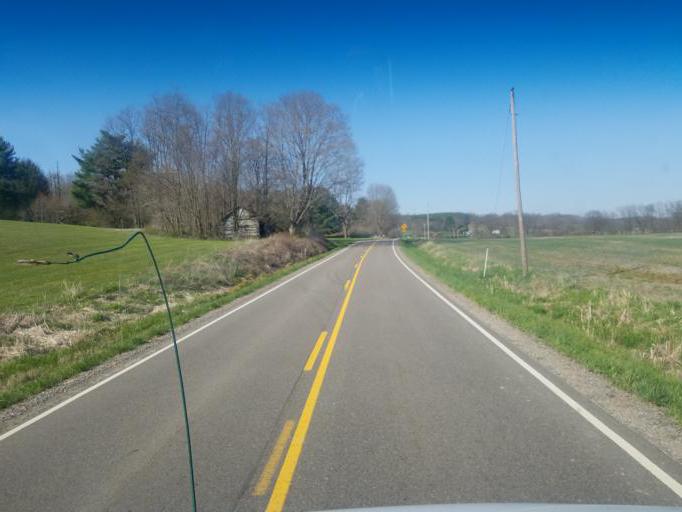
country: US
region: Ohio
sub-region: Muskingum County
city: Frazeysburg
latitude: 40.2336
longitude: -82.1589
